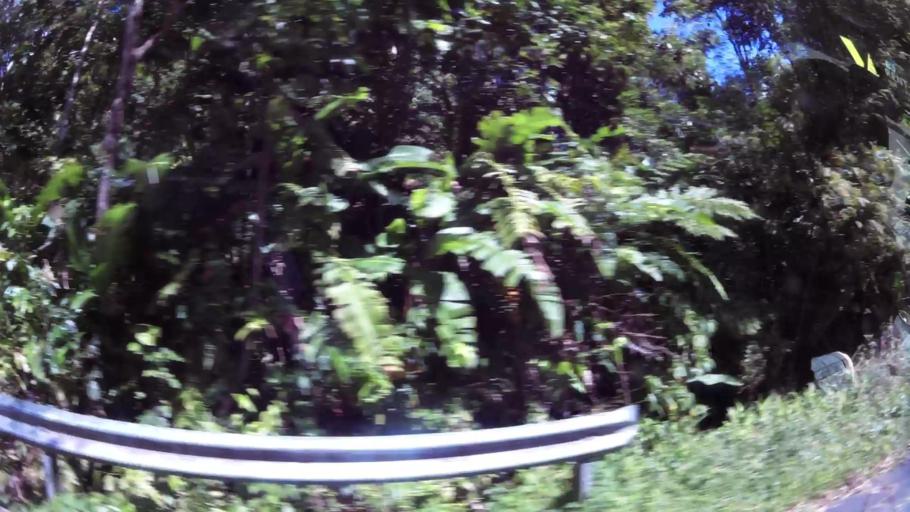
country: DM
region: Saint Paul
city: Pont Casse
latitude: 15.3522
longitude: -61.3613
